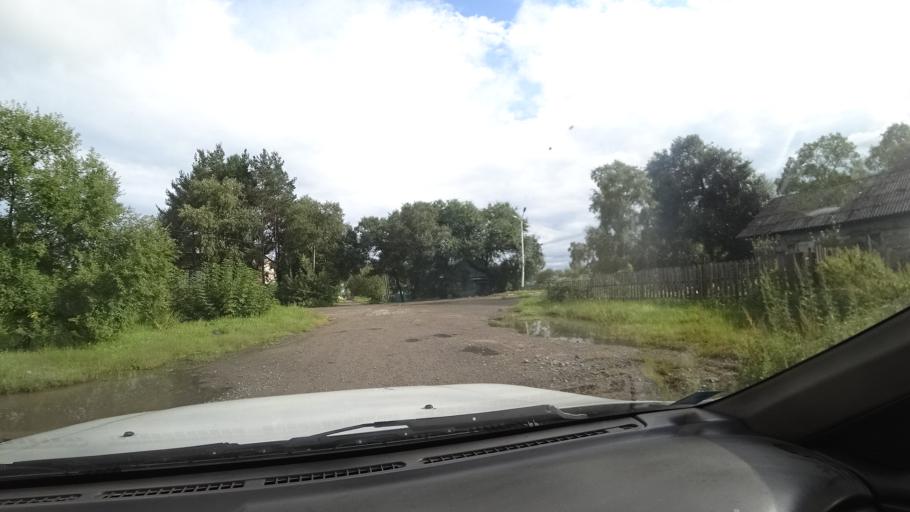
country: RU
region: Primorskiy
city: Dal'nerechensk
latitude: 45.9362
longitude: 133.7456
